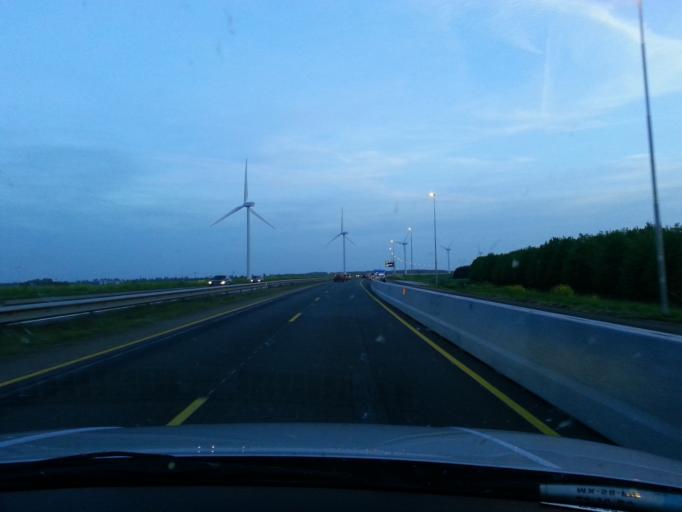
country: NL
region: Utrecht
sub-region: Gemeente Bunschoten
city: Spakenburg
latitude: 52.3291
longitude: 5.3466
